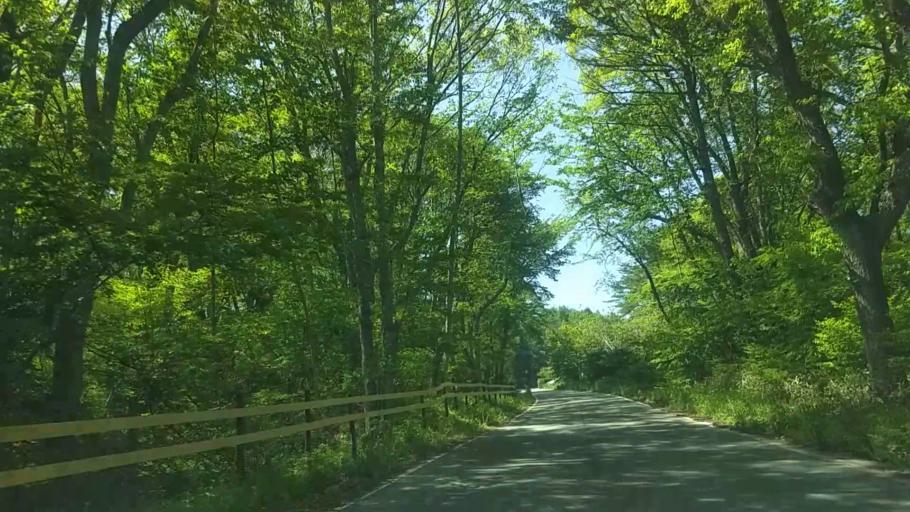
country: JP
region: Yamanashi
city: Nirasaki
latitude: 35.9012
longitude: 138.4483
